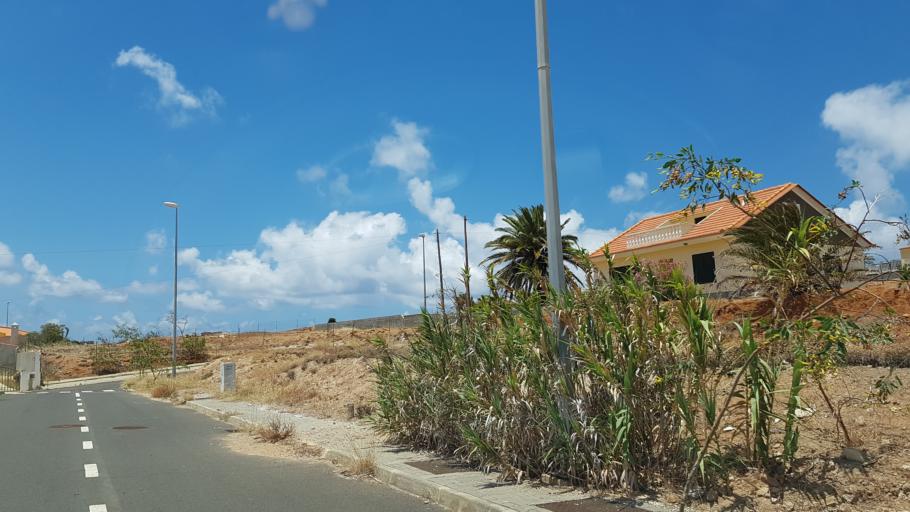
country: PT
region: Madeira
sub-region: Porto Santo
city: Vila de Porto Santo
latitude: 33.0563
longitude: -16.3654
